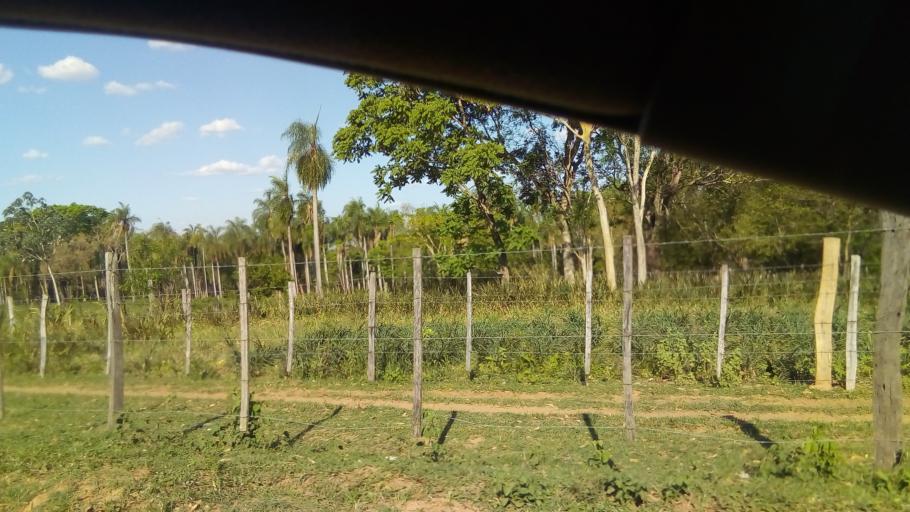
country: PY
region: Cordillera
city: Arroyos y Esteros
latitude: -24.9849
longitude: -57.1997
